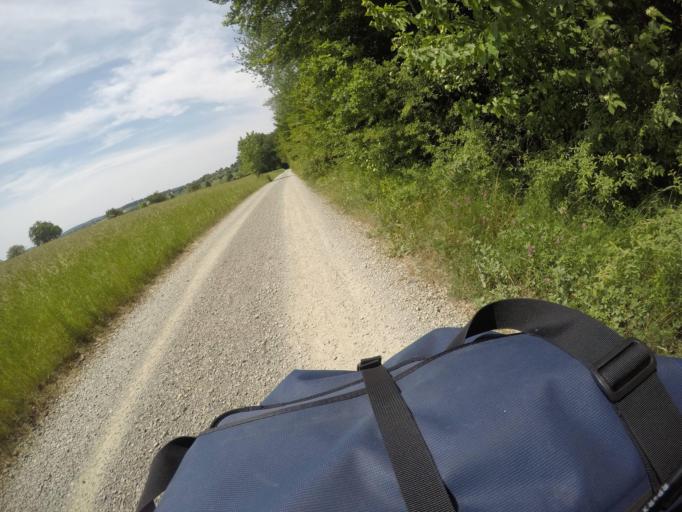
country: DE
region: Baden-Wuerttemberg
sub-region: Karlsruhe Region
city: Konigsbach-Stein
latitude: 48.9668
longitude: 8.5234
